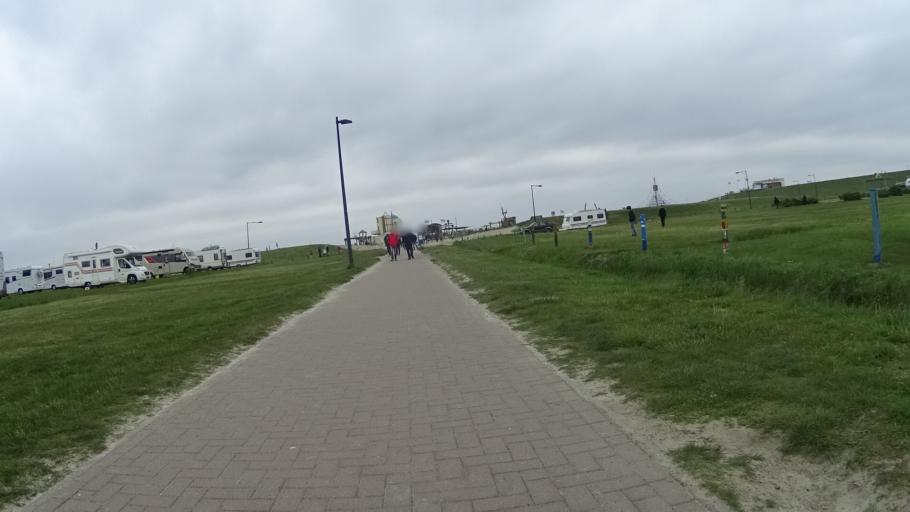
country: DE
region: Lower Saxony
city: Butjadingen
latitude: 53.5789
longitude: 8.2449
